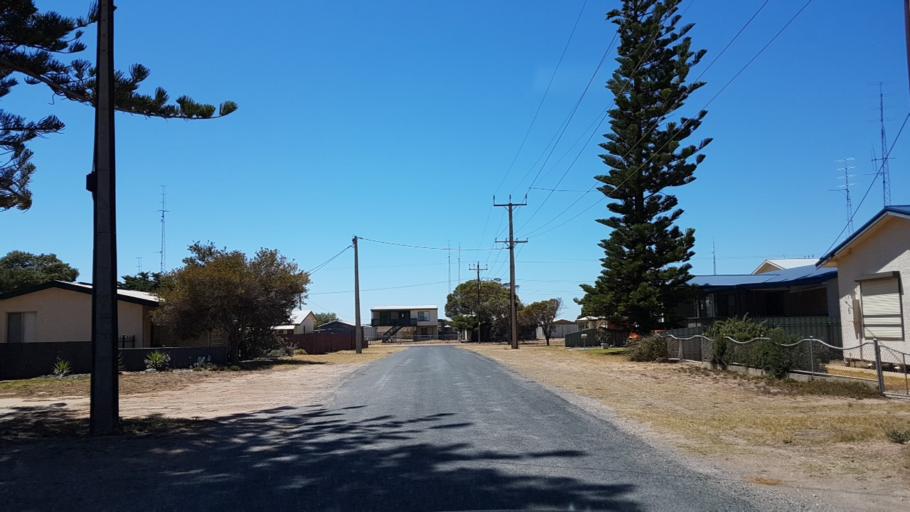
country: AU
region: South Australia
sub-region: Copper Coast
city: Wallaroo
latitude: -33.8996
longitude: 137.6295
